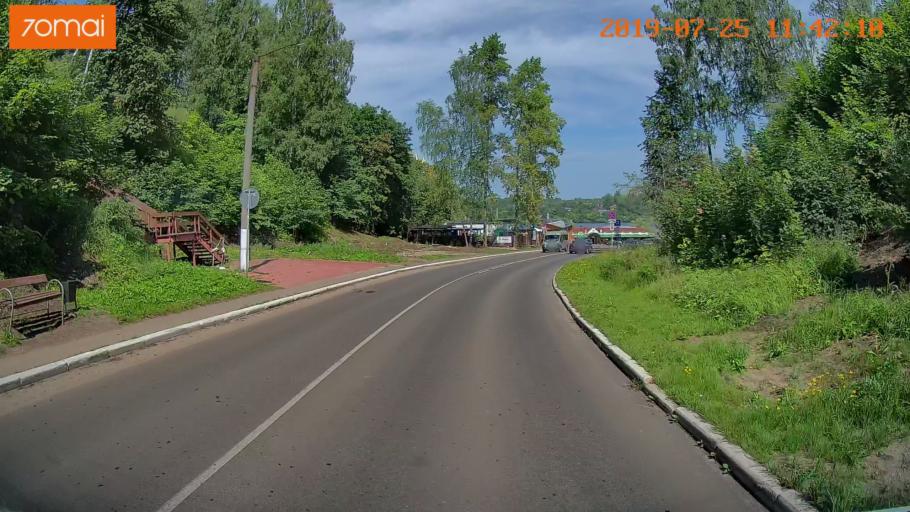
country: RU
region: Ivanovo
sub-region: Privolzhskiy Rayon
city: Ples
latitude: 57.4592
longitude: 41.5118
